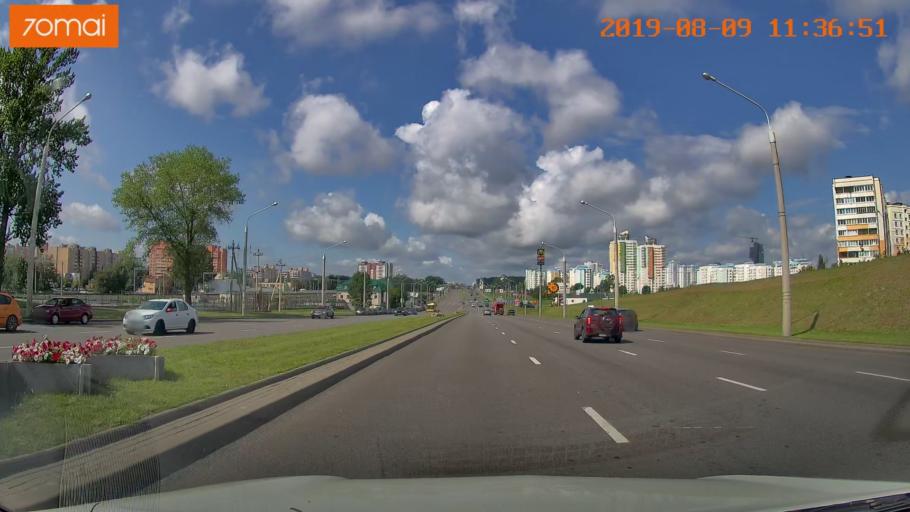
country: BY
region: Minsk
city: Novoye Medvezhino
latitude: 53.9298
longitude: 27.4949
